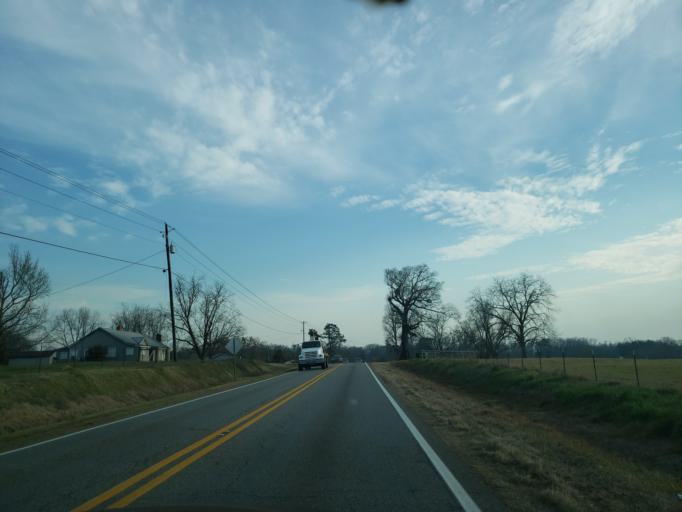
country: US
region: Alabama
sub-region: Hale County
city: Moundville
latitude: 32.9743
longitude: -87.6245
